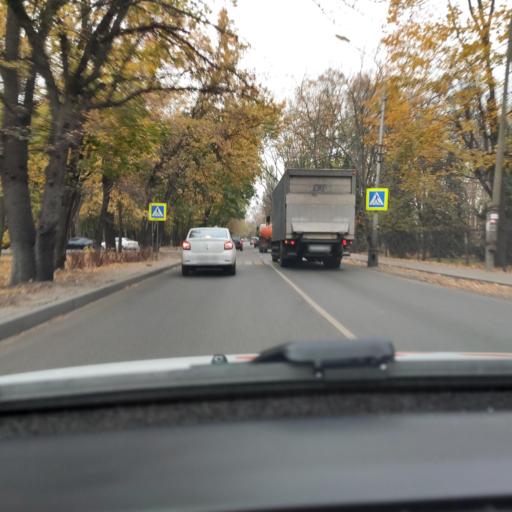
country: RU
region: Voronezj
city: Voronezh
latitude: 51.7127
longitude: 39.2246
